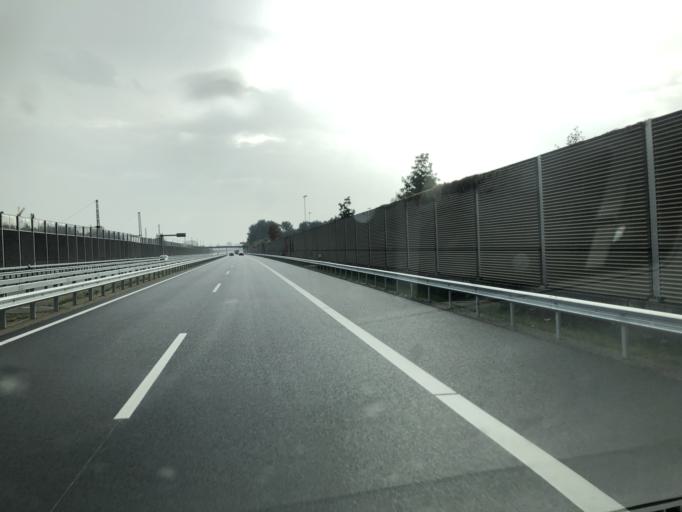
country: DE
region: Hamburg
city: Kleiner Grasbrook
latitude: 53.4944
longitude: 10.0046
